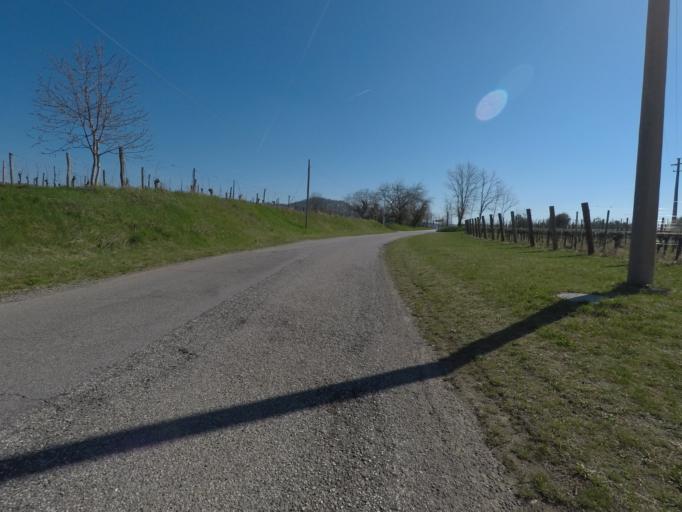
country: IT
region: Friuli Venezia Giulia
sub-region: Provincia di Gorizia
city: Cormons
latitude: 45.9661
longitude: 13.4469
